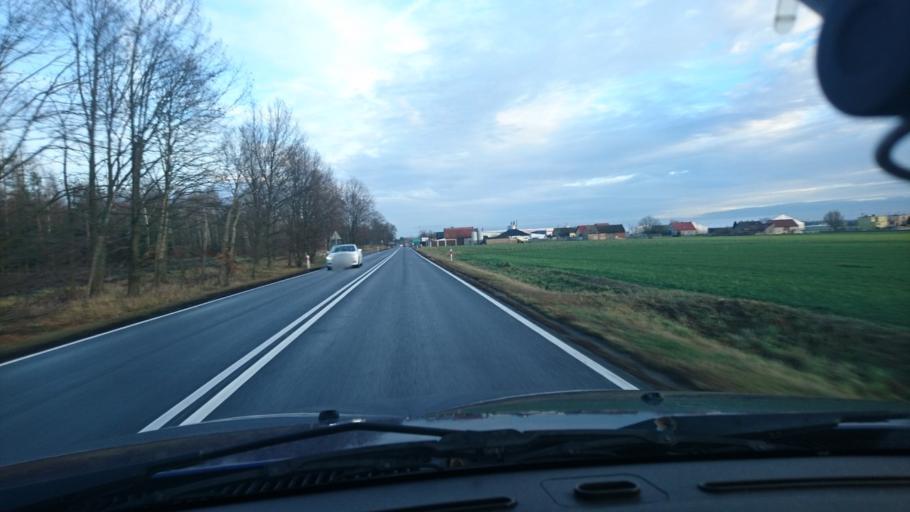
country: PL
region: Greater Poland Voivodeship
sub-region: Powiat kepinski
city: Leka Opatowska
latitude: 51.2250
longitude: 18.0915
